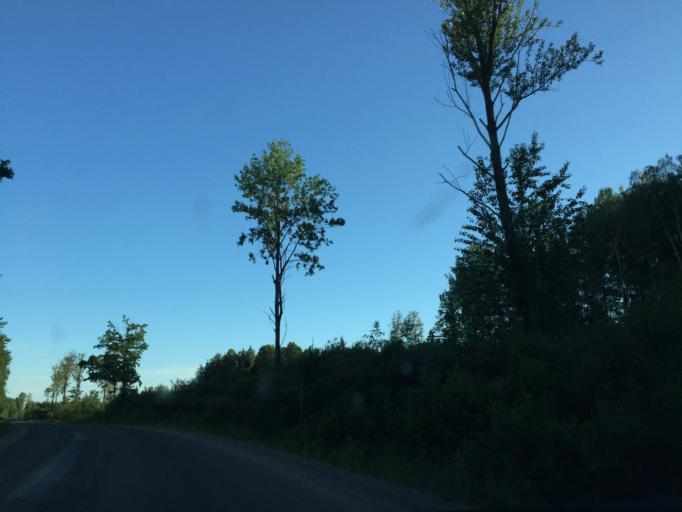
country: LV
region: Broceni
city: Broceni
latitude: 56.7319
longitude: 22.5044
